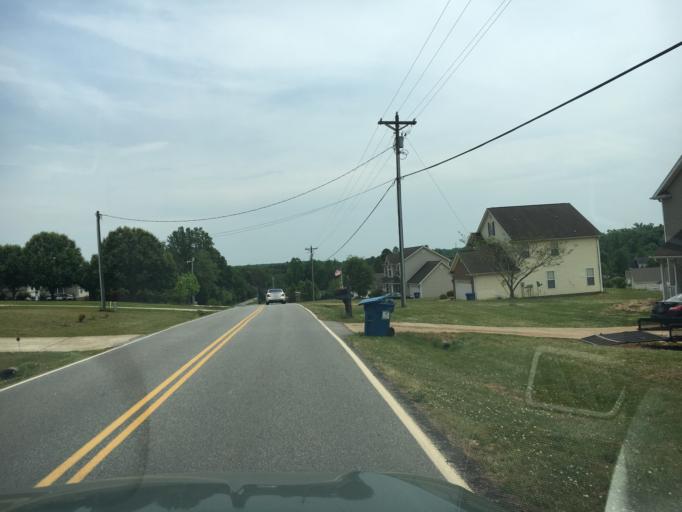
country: US
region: South Carolina
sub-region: Spartanburg County
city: Wellford
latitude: 34.9936
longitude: -82.1057
